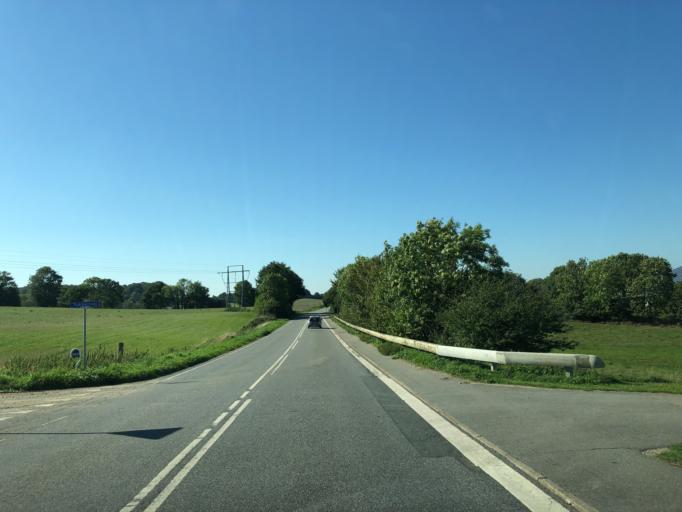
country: DK
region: South Denmark
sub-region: Aabenraa Kommune
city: Aabenraa
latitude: 55.0151
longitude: 9.4798
